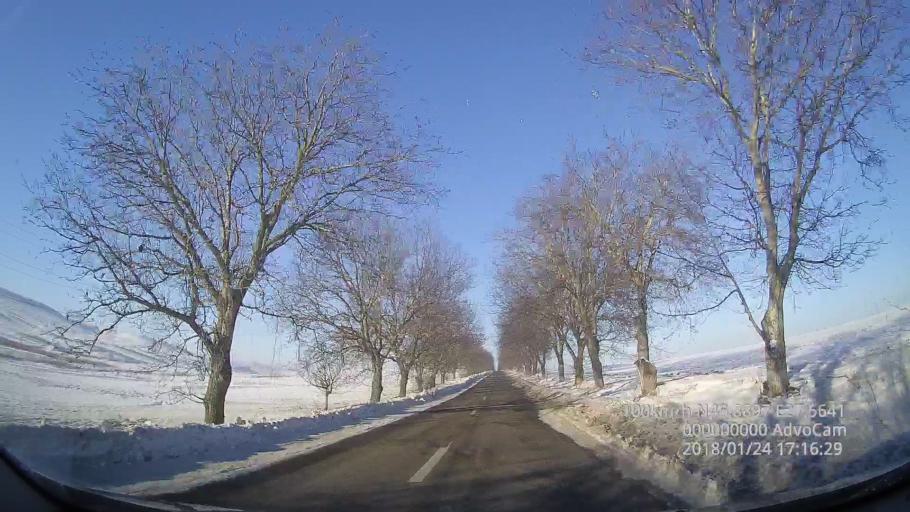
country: RO
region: Iasi
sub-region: Comuna Scanteia
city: Scanteia
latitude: 46.8905
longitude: 27.5641
